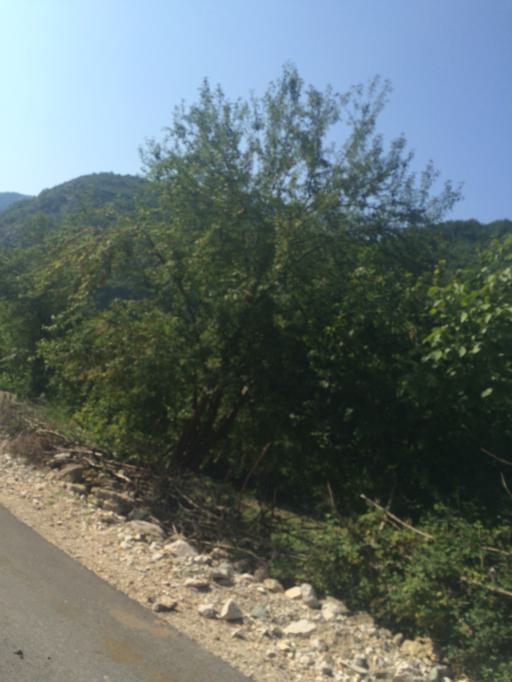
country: AL
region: Kukes
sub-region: Rrethi i Tropojes
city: Valbone
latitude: 42.4412
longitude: 19.9598
